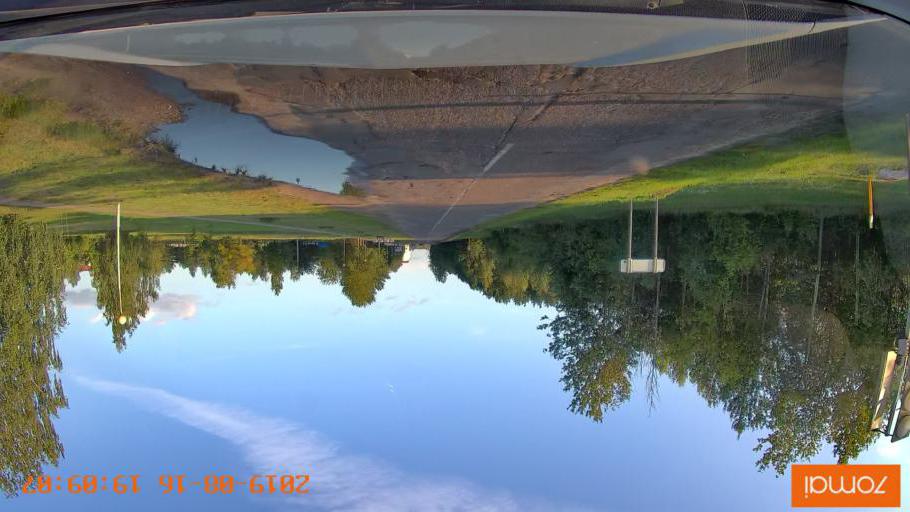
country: BY
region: Mogilev
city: Asipovichy
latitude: 53.3158
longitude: 28.6326
